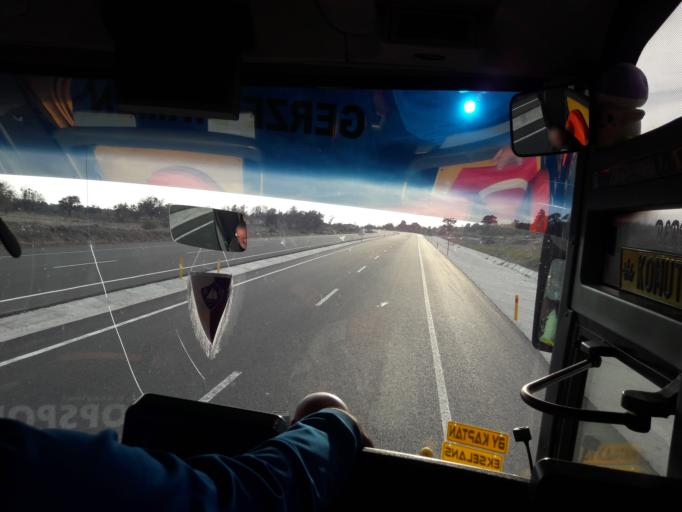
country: TR
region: Cankiri
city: Ilgaz
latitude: 40.8588
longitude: 33.6211
